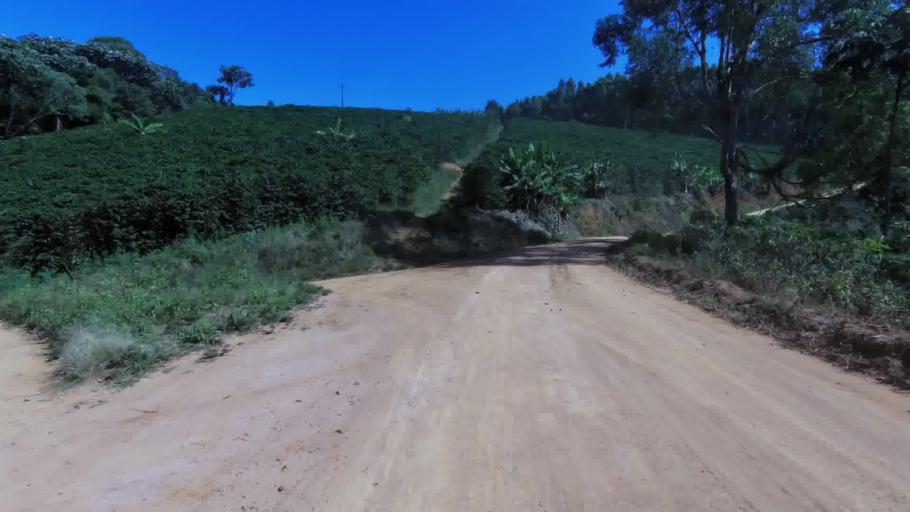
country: BR
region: Espirito Santo
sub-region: Alfredo Chaves
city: Alfredo Chaves
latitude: -20.5216
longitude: -40.8696
